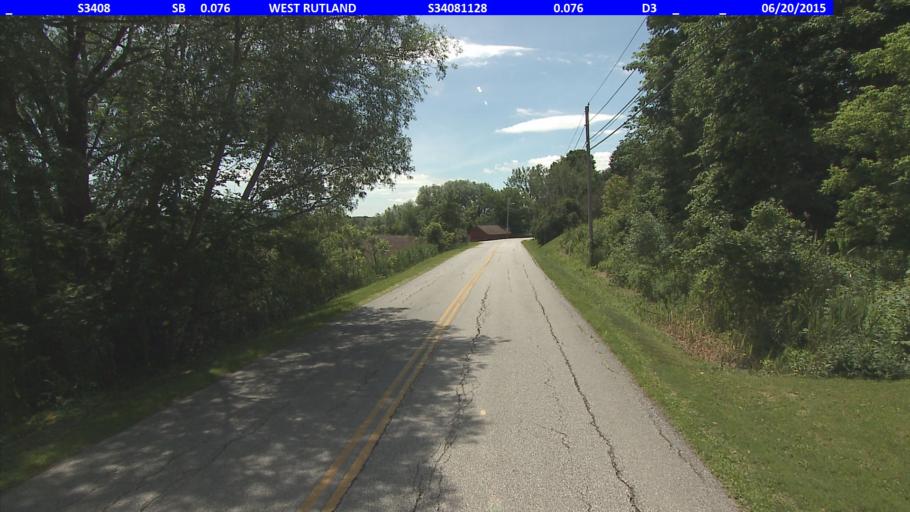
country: US
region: Vermont
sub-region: Rutland County
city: West Rutland
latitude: 43.6114
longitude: -73.0627
